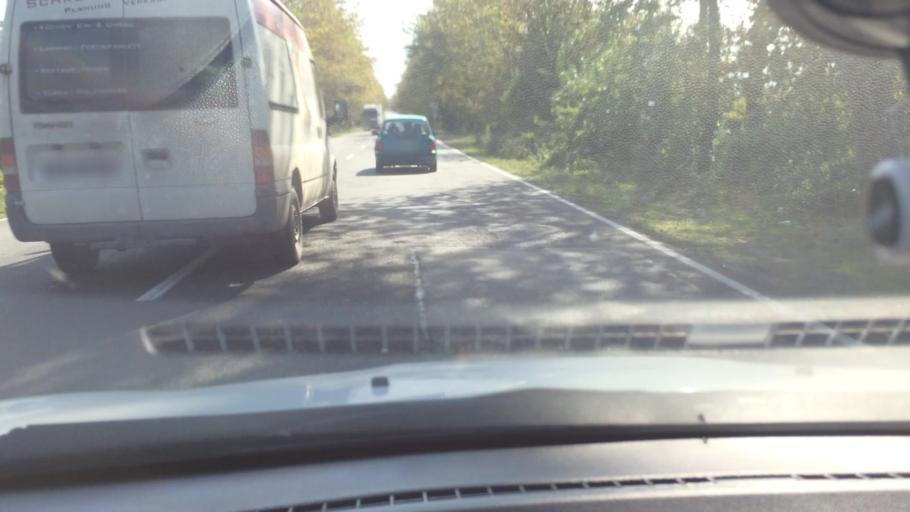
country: GE
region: Guria
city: Urek'i
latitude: 42.0156
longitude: 41.7704
